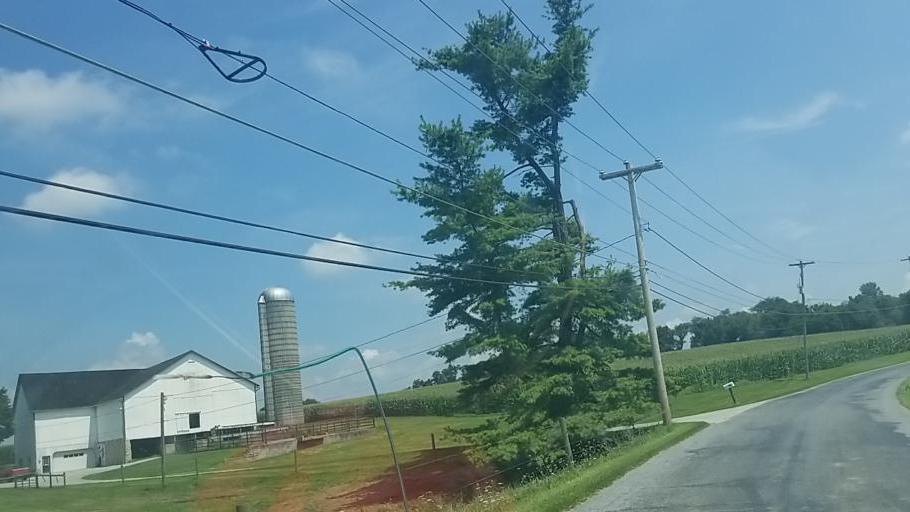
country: US
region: Pennsylvania
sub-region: Chester County
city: Parkesburg
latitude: 39.8909
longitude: -75.9306
